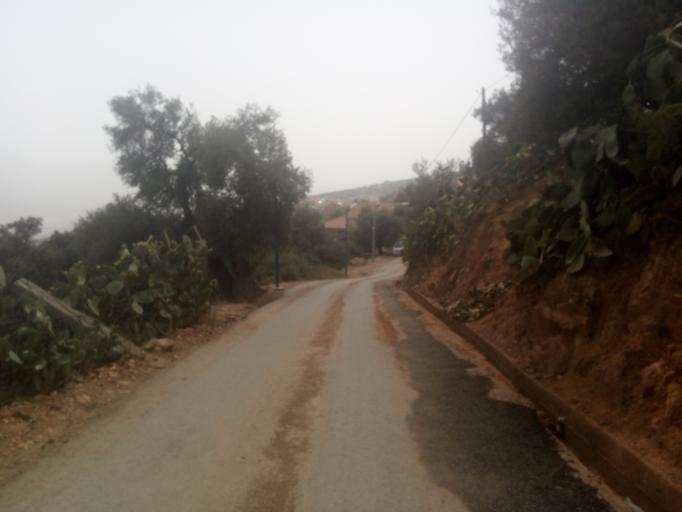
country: DZ
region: Tizi Ouzou
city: Chemini
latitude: 36.6034
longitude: 4.6381
